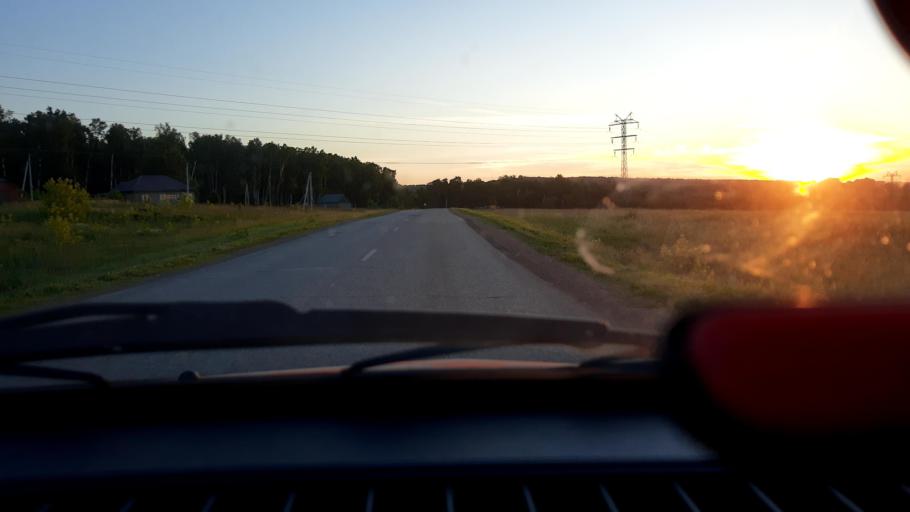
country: RU
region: Bashkortostan
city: Avdon
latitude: 54.6334
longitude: 55.6967
